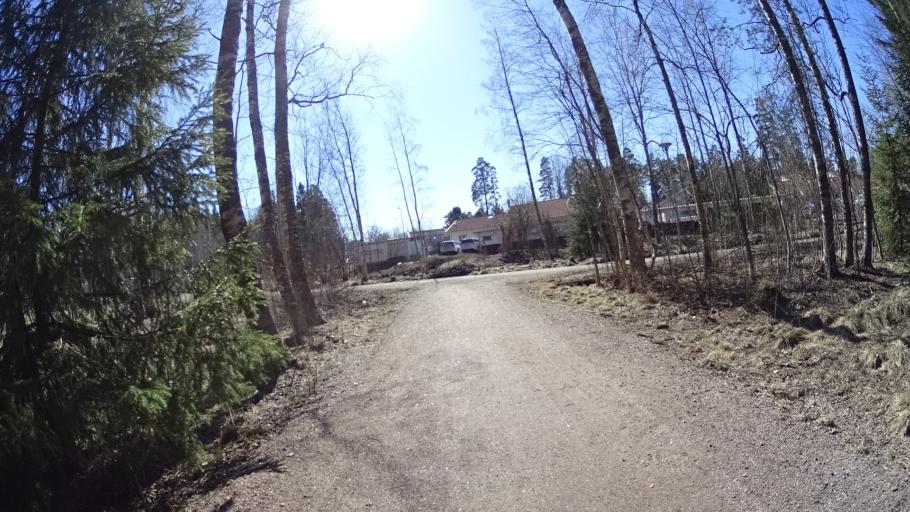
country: FI
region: Uusimaa
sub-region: Helsinki
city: Koukkuniemi
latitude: 60.1458
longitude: 24.6995
